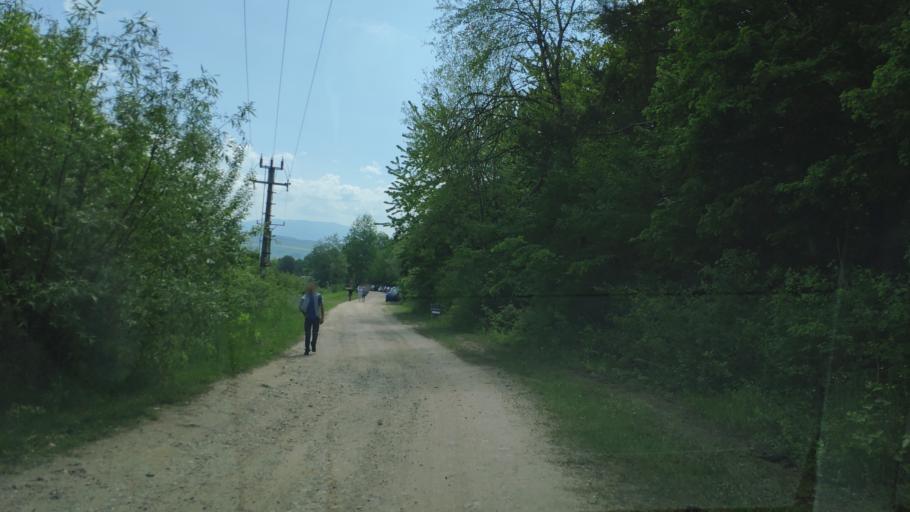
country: SK
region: Kosicky
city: Kosice
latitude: 48.7722
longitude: 21.2967
